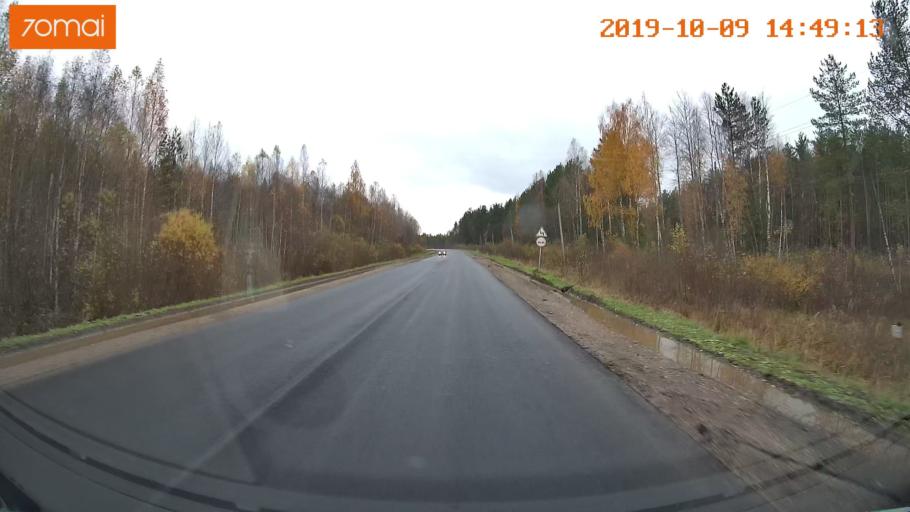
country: RU
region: Kostroma
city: Chistyye Bory
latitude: 58.3959
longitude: 41.5800
